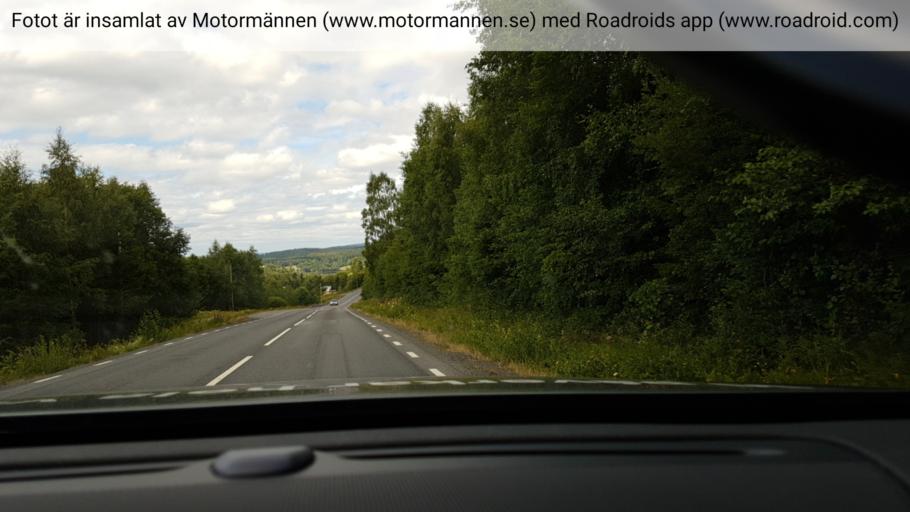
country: SE
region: Vaesternorrland
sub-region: Kramfors Kommun
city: Nordingra
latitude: 62.9272
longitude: 18.1316
